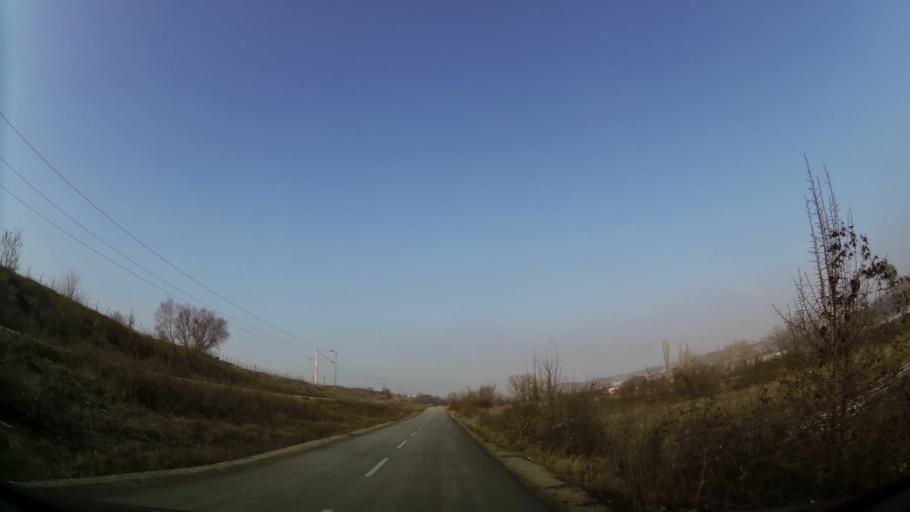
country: MK
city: Miladinovci
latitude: 41.9928
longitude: 21.6551
